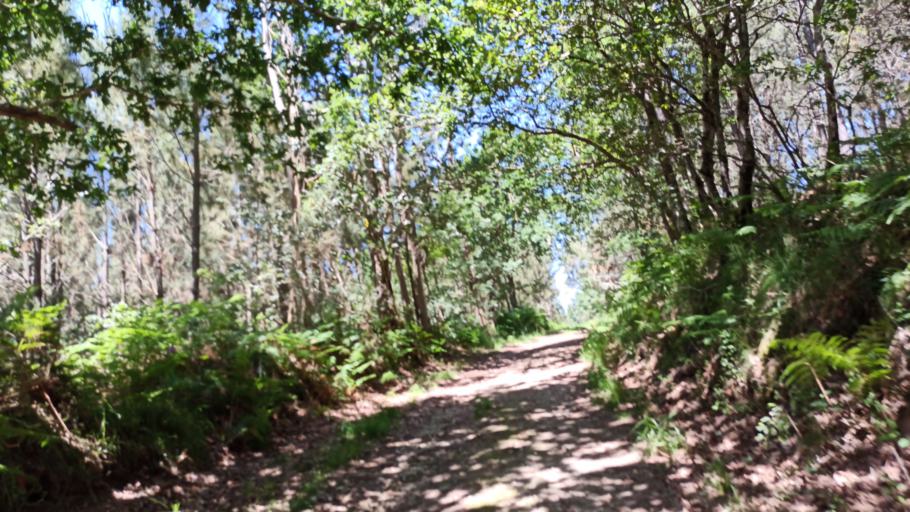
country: ES
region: Galicia
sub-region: Provincia da Coruna
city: Negreira
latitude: 42.9128
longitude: -8.7243
